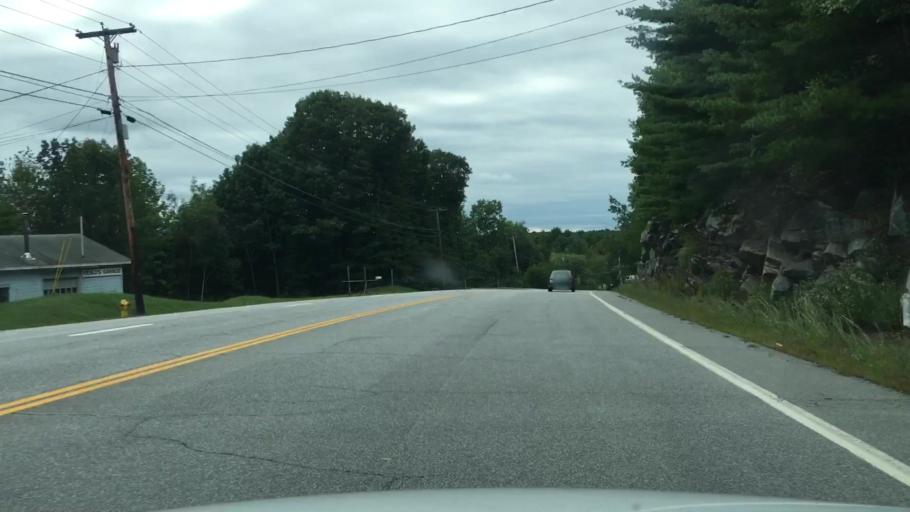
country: US
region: Maine
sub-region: Kennebec County
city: Gardiner
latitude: 44.2109
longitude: -69.8123
